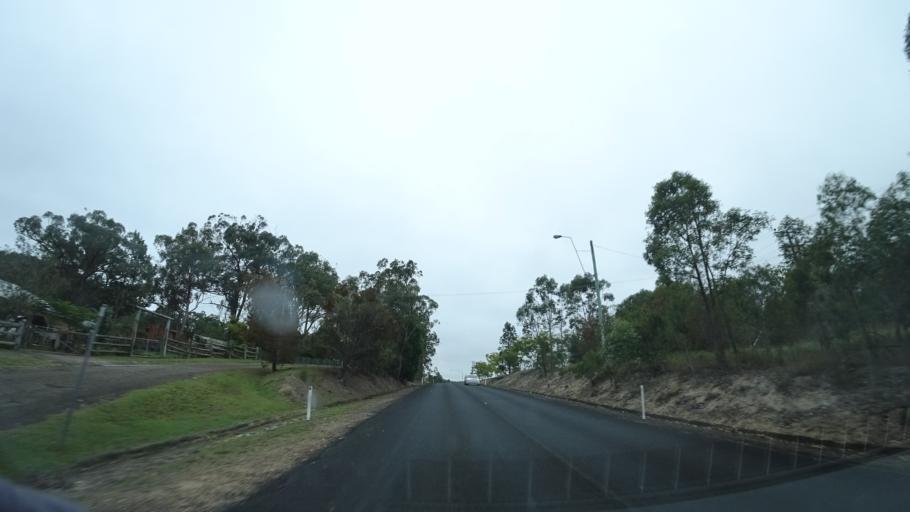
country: AU
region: Queensland
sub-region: Tablelands
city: Atherton
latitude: -17.3690
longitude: 145.3878
